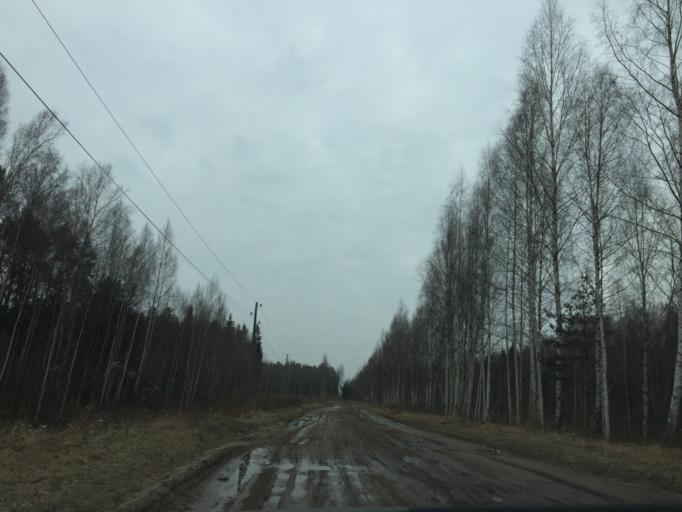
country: LV
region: Kekava
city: Balozi
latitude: 56.7846
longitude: 24.1260
